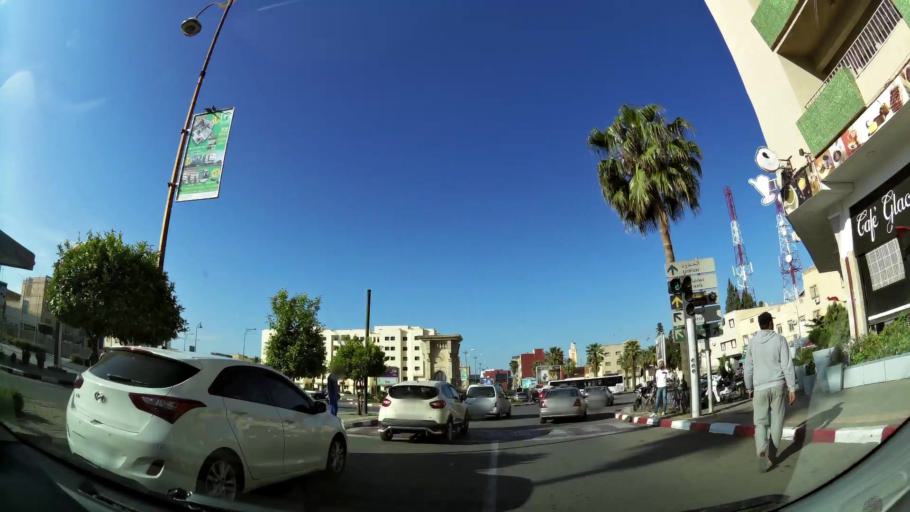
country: MA
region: Oriental
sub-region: Oujda-Angad
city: Oujda
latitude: 34.6916
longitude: -1.9076
